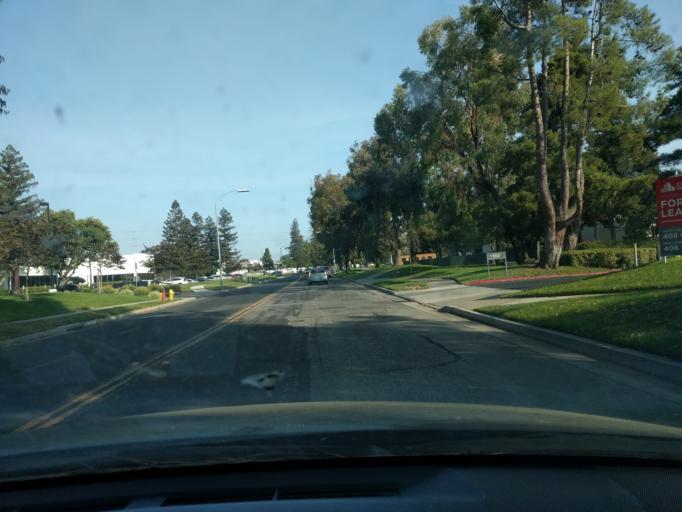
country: US
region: California
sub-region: Santa Clara County
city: Milpitas
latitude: 37.3924
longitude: -121.9226
